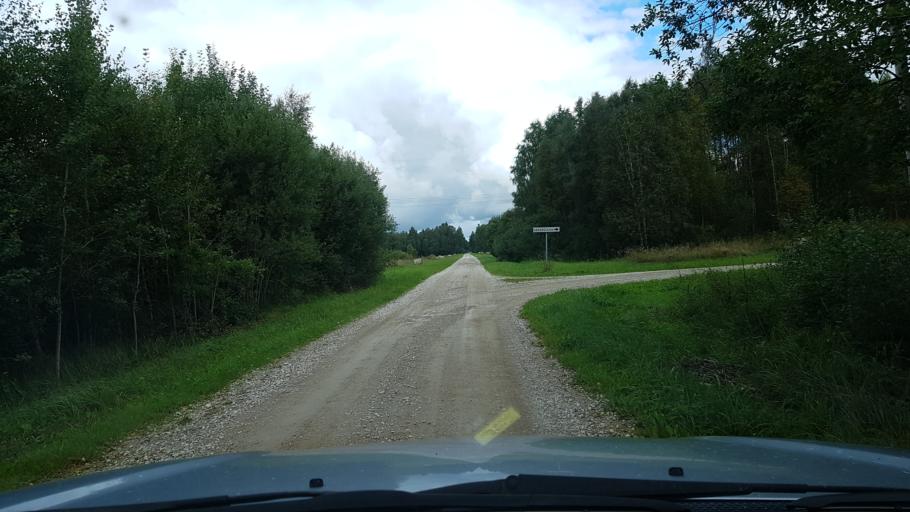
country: EE
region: Harju
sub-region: Rae vald
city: Vaida
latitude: 59.2693
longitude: 25.0478
